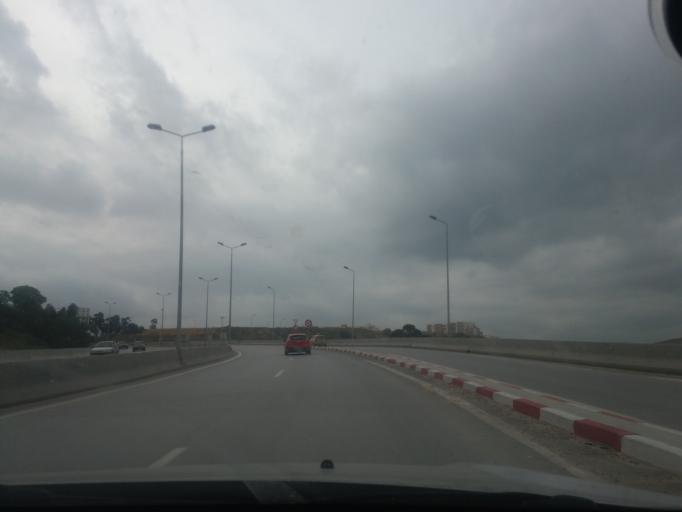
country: TN
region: Ariana
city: Ariana
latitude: 36.8662
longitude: 10.1807
